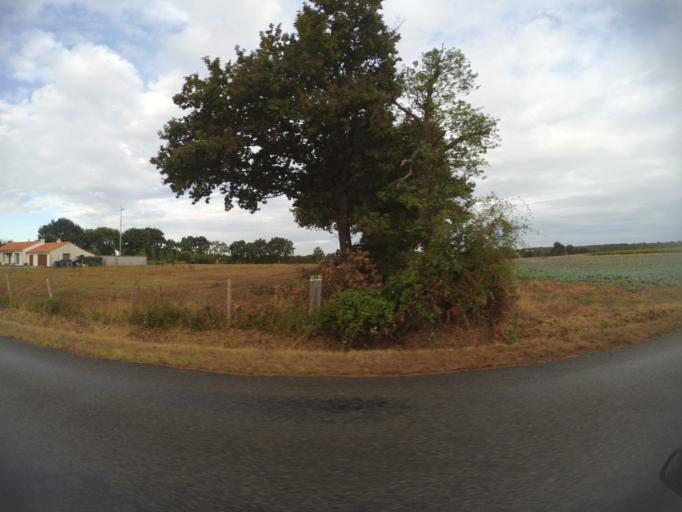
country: FR
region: Pays de la Loire
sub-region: Departement de la Loire-Atlantique
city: Aigrefeuille-sur-Maine
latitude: 47.0641
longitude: -1.4063
